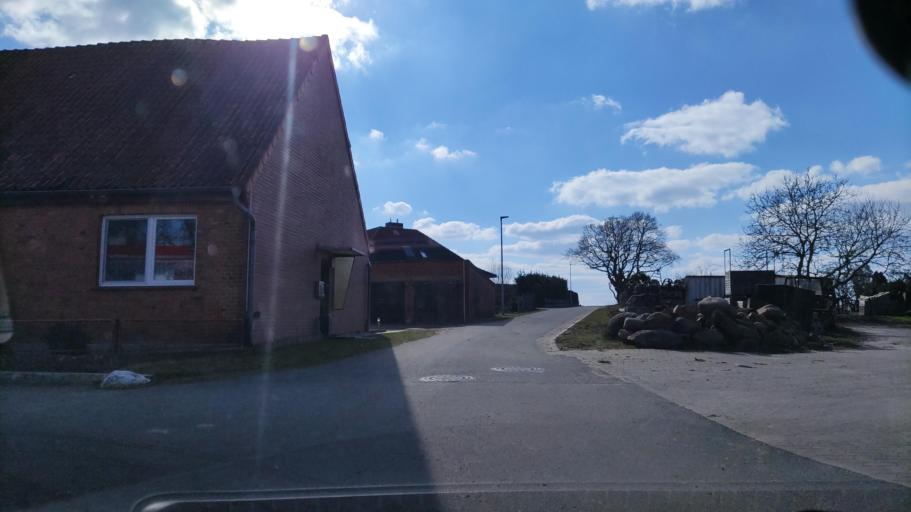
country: DE
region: Lower Saxony
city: Jelmstorf
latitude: 53.0990
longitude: 10.5227
